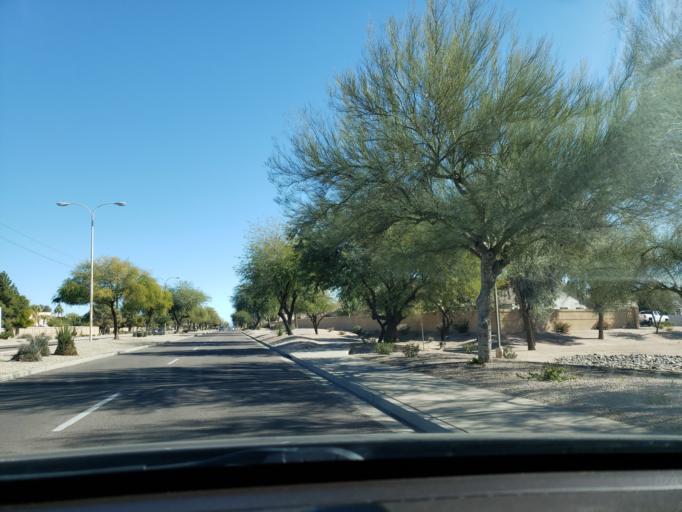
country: US
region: Arizona
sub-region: Maricopa County
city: Chandler
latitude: 33.3207
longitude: -111.8179
